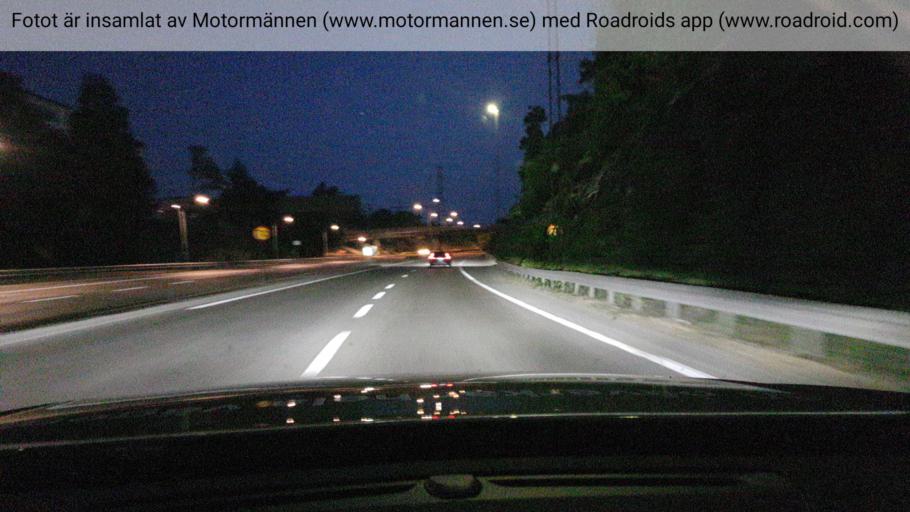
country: SE
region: Stockholm
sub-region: Stockholms Kommun
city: Arsta
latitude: 59.2848
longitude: 18.0461
